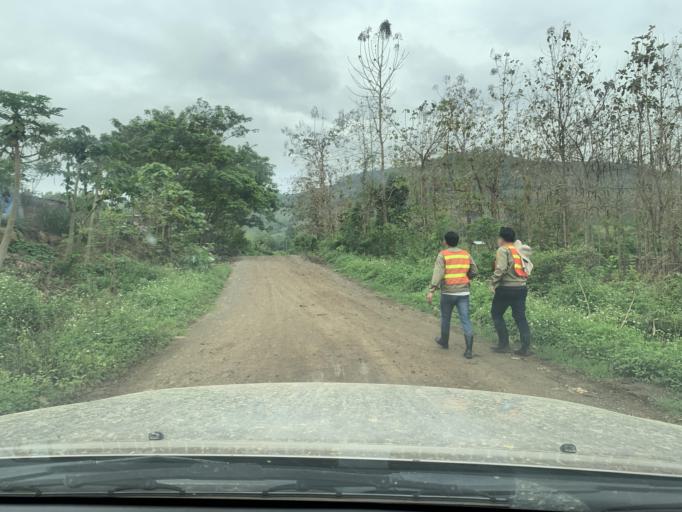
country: TH
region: Uttaradit
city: Ban Khok
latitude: 18.3946
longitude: 101.4295
